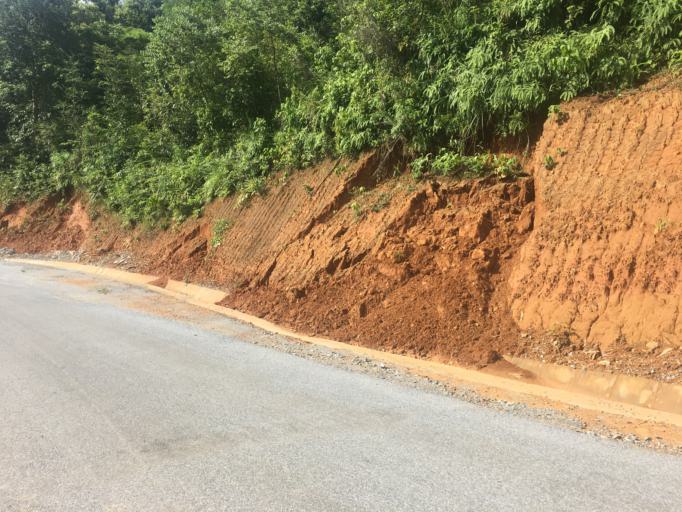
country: VN
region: Ha Giang
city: Thanh Pho Ha Giang
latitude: 22.8799
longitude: 105.0420
